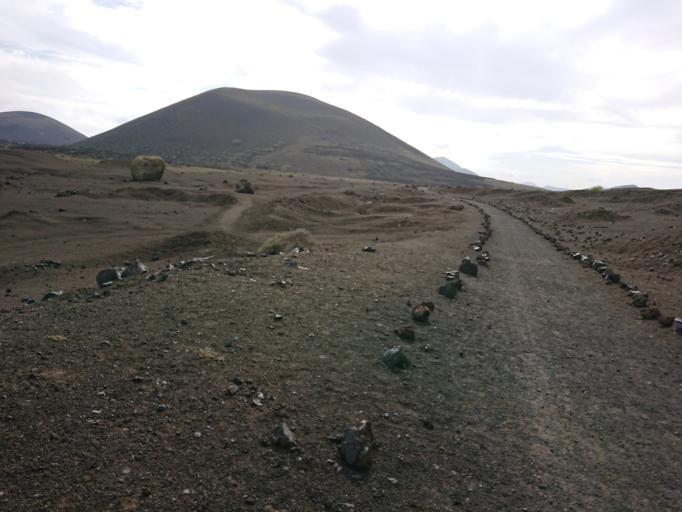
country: ES
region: Canary Islands
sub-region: Provincia de Las Palmas
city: Tias
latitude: 29.0047
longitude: -13.6761
